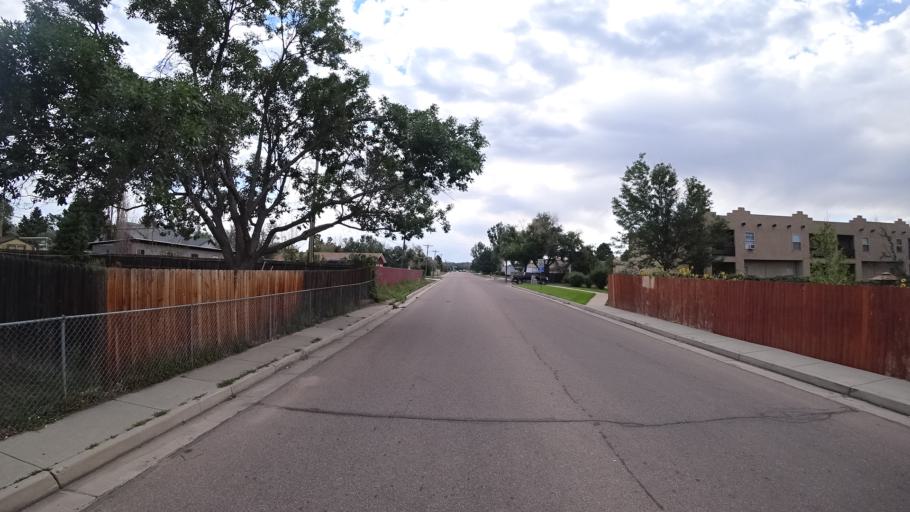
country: US
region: Colorado
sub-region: El Paso County
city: Cimarron Hills
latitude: 38.8978
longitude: -104.7524
